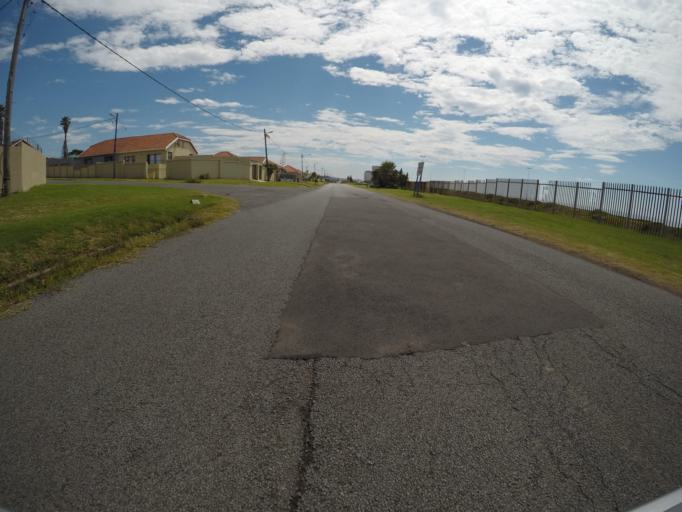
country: ZA
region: Eastern Cape
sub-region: Buffalo City Metropolitan Municipality
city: East London
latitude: -33.0385
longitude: 27.9057
